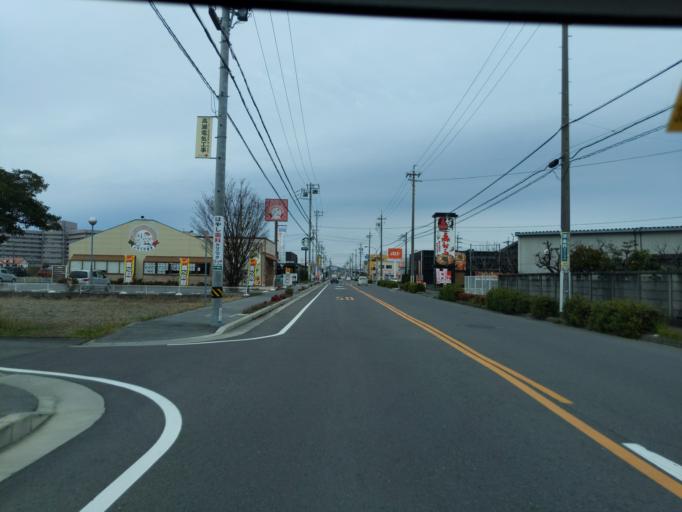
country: JP
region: Aichi
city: Kasugai
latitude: 35.2672
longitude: 136.9721
